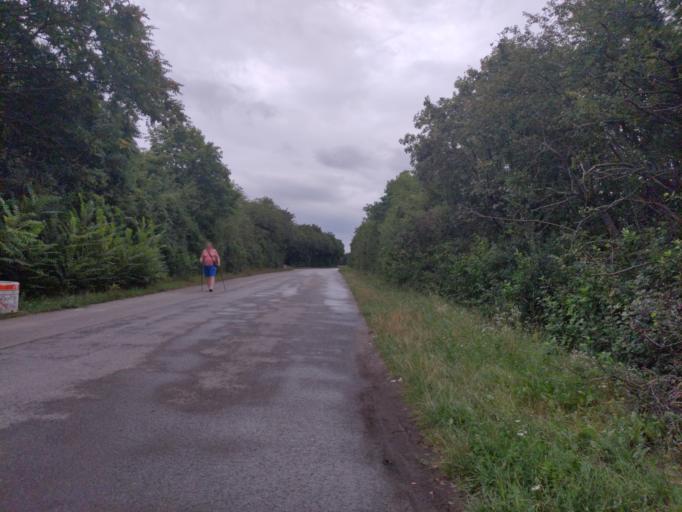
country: AT
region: Vienna
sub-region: Wien Stadt
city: Vienna
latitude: 48.2536
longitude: 16.3816
